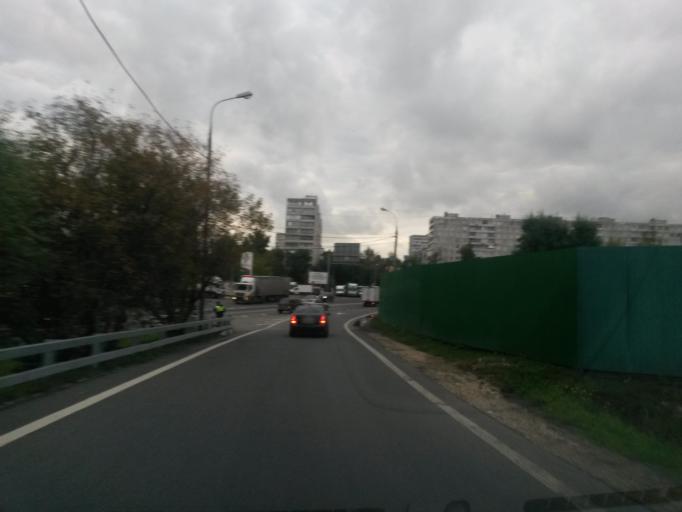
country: RU
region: Moscow
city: Zagor'ye
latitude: 55.5733
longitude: 37.6534
